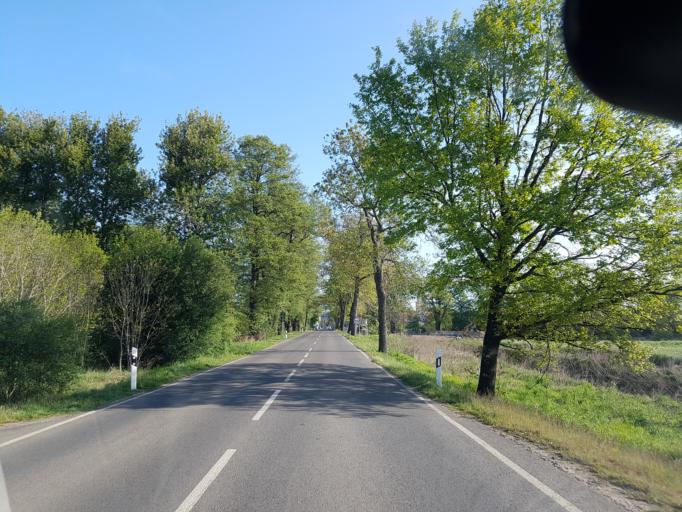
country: DE
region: Brandenburg
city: Altdobern
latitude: 51.6473
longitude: 14.0342
